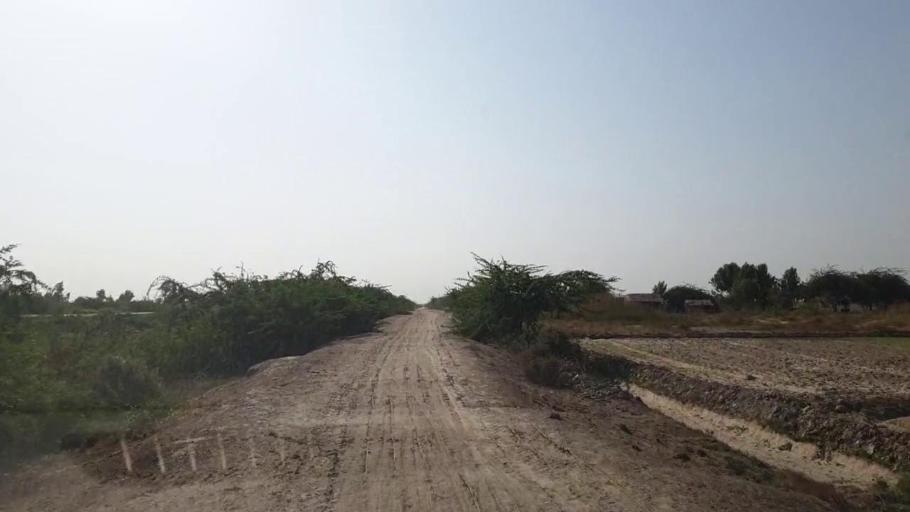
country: PK
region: Sindh
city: Kadhan
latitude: 24.5770
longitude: 69.0808
